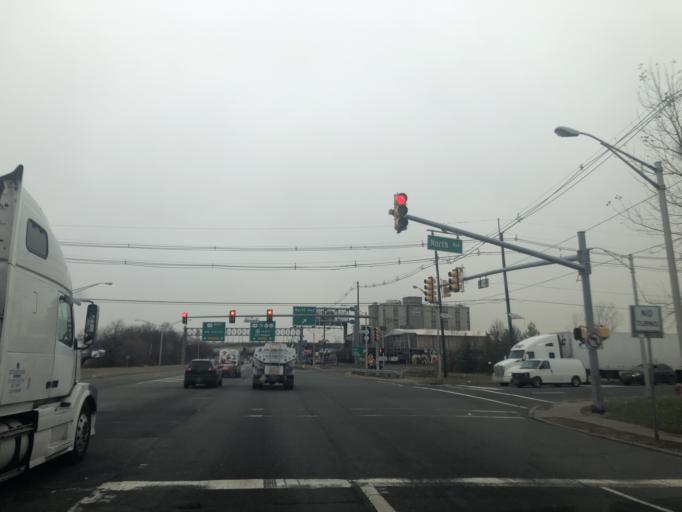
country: US
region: New Jersey
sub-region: Union County
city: Elizabeth
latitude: 40.6770
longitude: -74.1973
